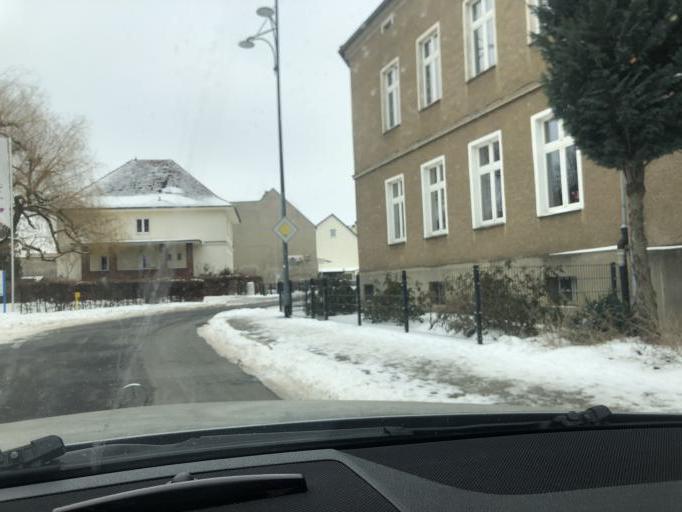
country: DE
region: Brandenburg
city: Guben
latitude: 51.9477
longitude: 14.7148
